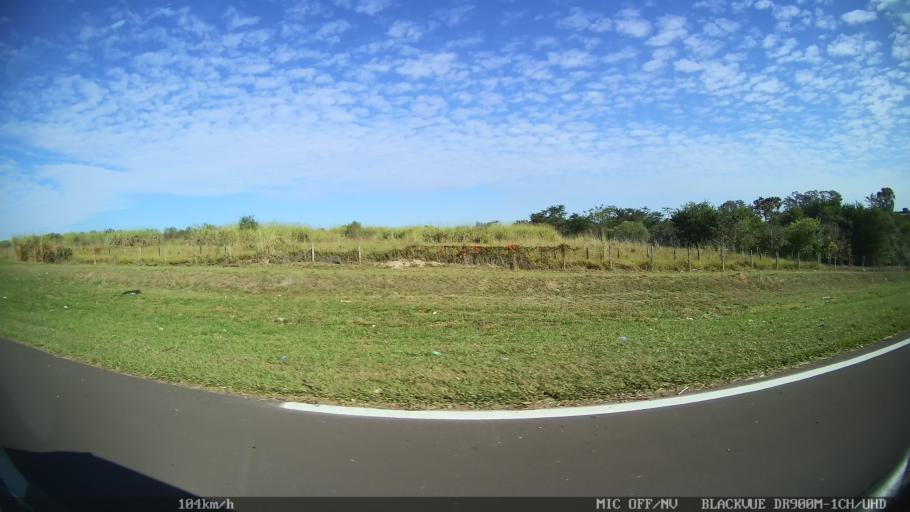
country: BR
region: Sao Paulo
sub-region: Nova Odessa
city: Nova Odessa
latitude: -22.7539
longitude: -47.2781
